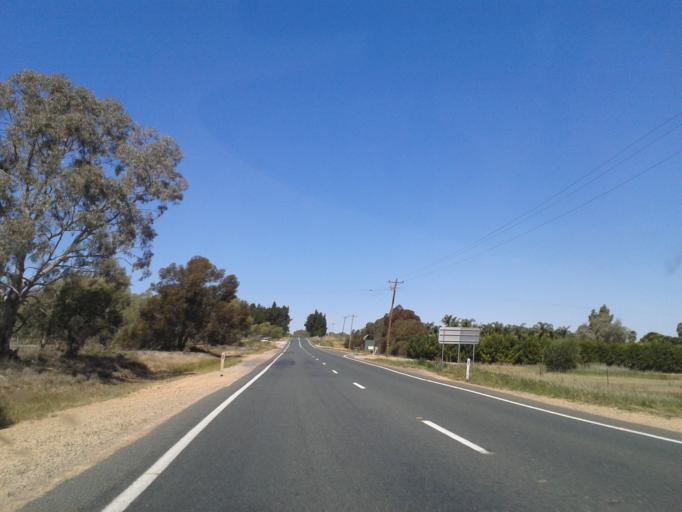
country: AU
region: New South Wales
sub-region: Wentworth
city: Gol Gol
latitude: -34.2332
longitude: 142.2489
